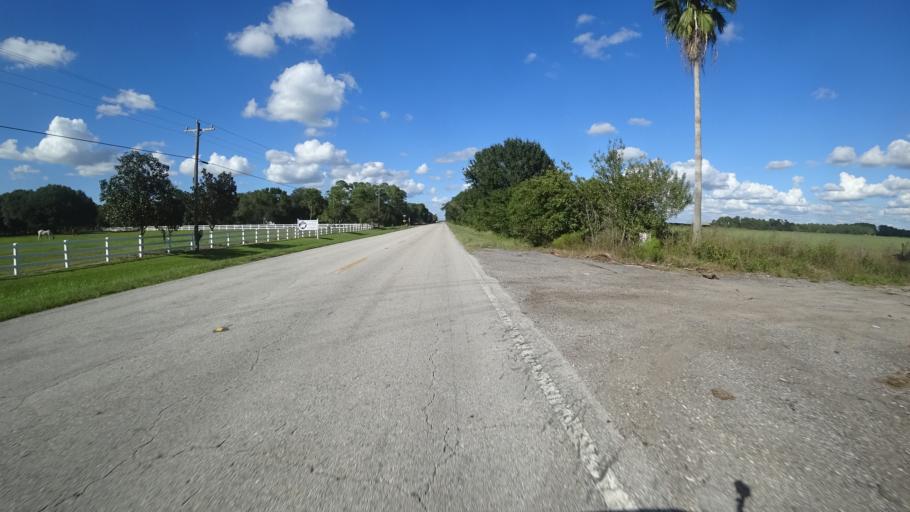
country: US
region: Florida
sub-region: Sarasota County
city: The Meadows
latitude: 27.4563
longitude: -82.3033
